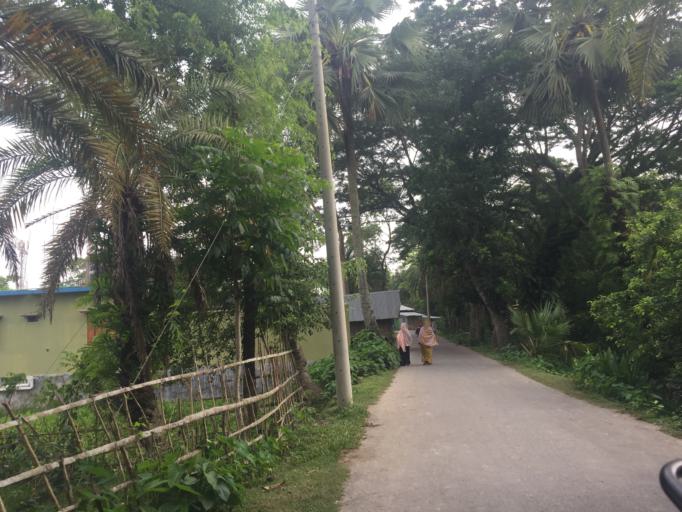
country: BD
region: Barisal
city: Mathba
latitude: 22.2147
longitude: 89.9184
